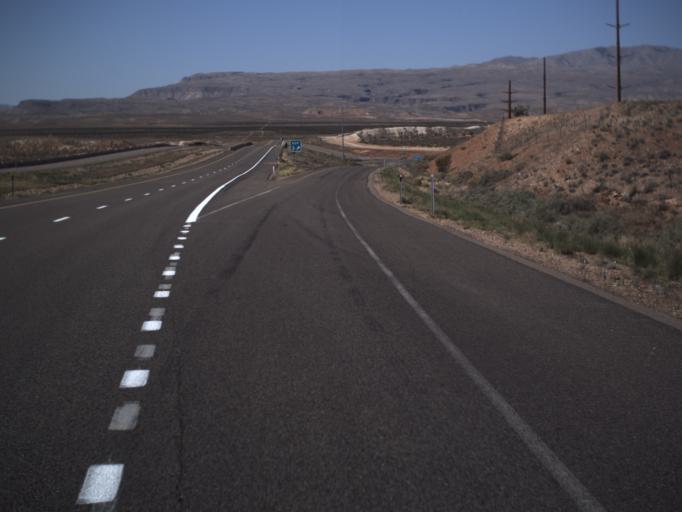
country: US
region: Utah
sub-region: Washington County
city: Saint George
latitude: 37.0008
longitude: -113.5550
